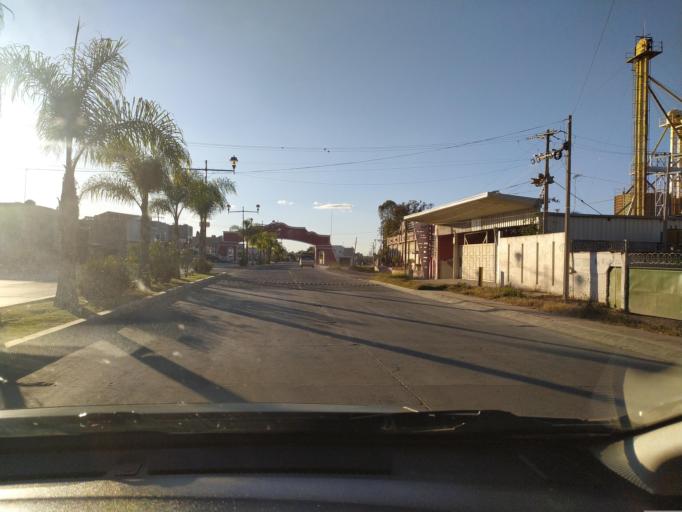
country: MX
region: Jalisco
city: San Julian
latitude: 21.0081
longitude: -102.1656
